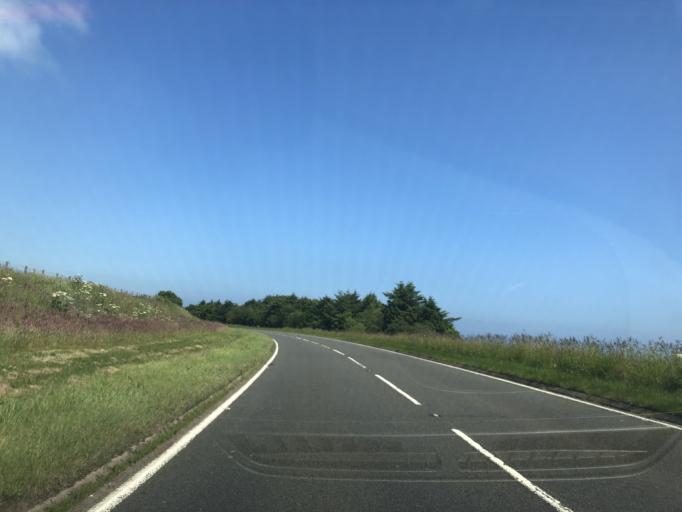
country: GB
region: Scotland
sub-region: Aberdeenshire
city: Stonehaven
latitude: 56.9224
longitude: -2.2062
